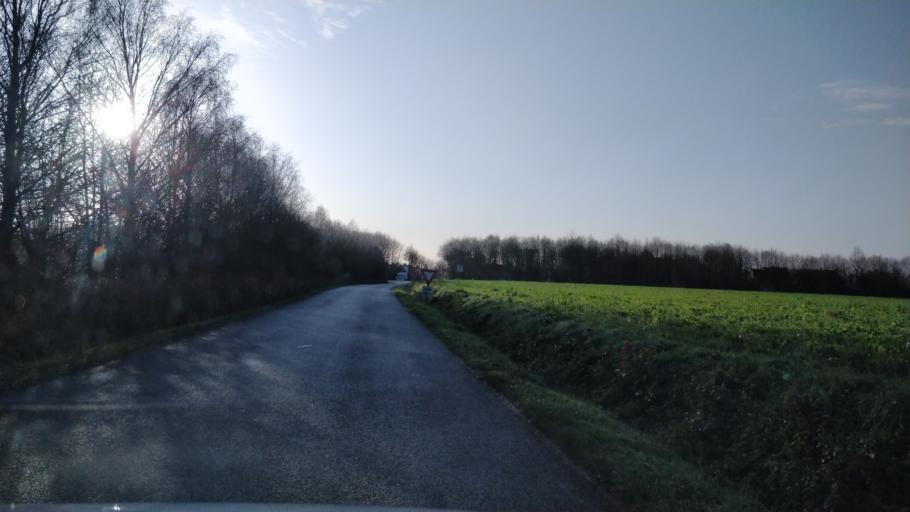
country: FR
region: Brittany
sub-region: Departement d'Ille-et-Vilaine
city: Chavagne
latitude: 48.0611
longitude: -1.7889
